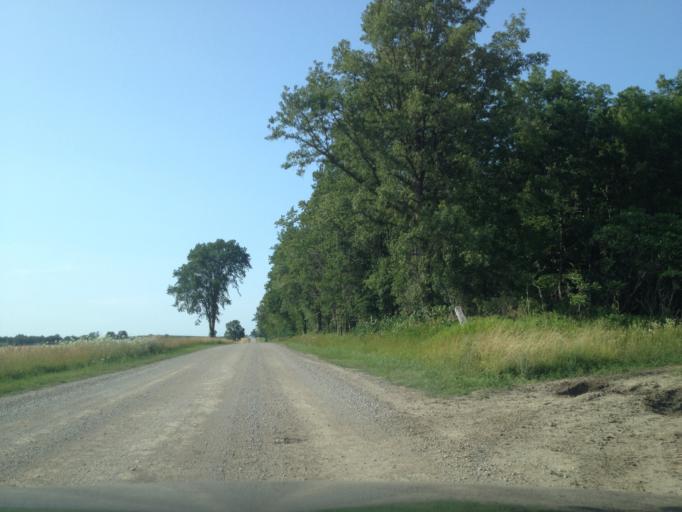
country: CA
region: Ontario
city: Ingersoll
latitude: 42.9504
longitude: -80.7721
